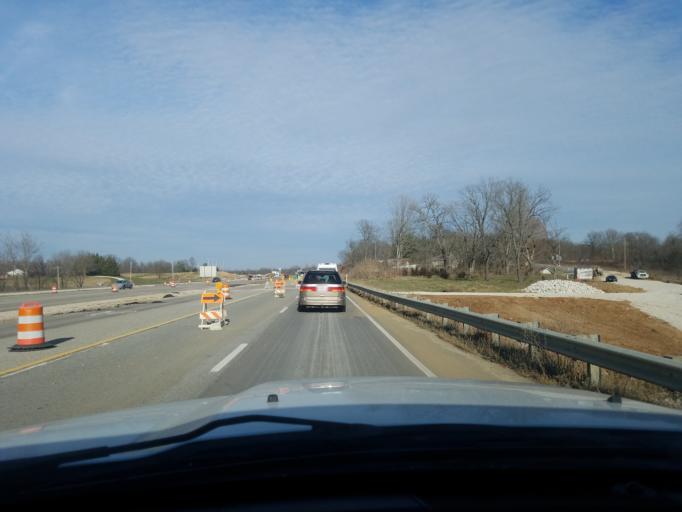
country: US
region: Indiana
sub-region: Monroe County
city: Bloomington
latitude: 39.2559
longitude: -86.5261
